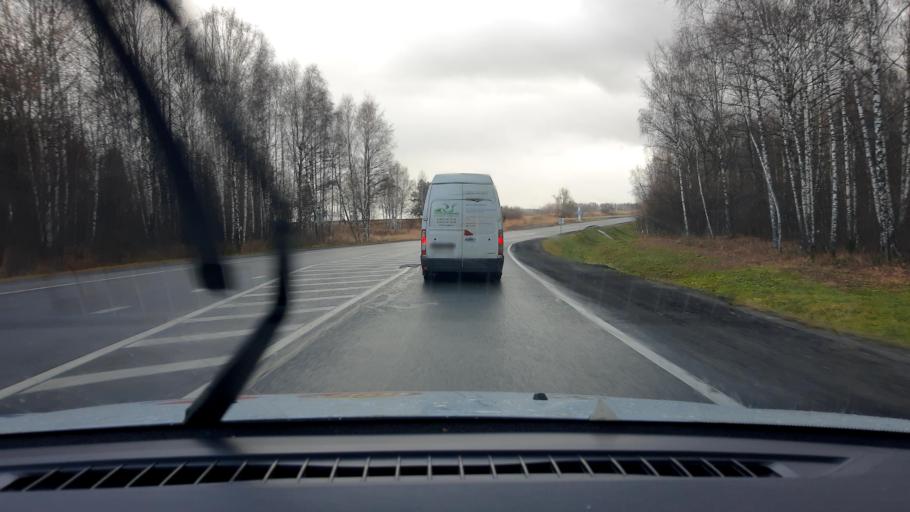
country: RU
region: Nizjnij Novgorod
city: Pervoye Maya
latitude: 56.0023
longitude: 44.7217
